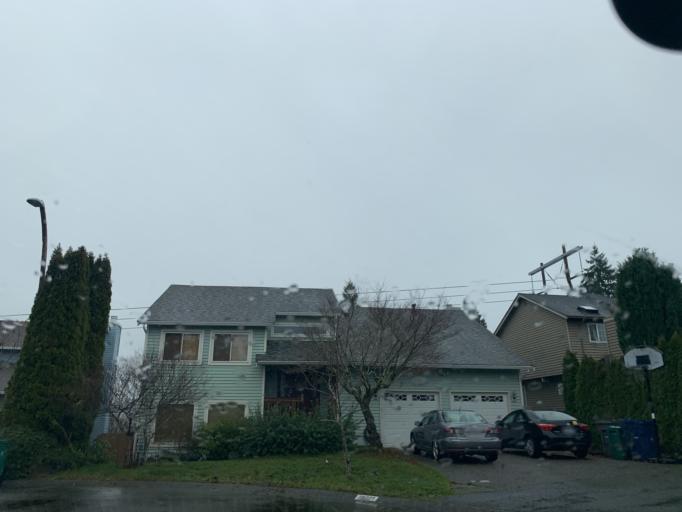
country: US
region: Washington
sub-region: King County
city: Woodinville
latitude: 47.7488
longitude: -122.1716
